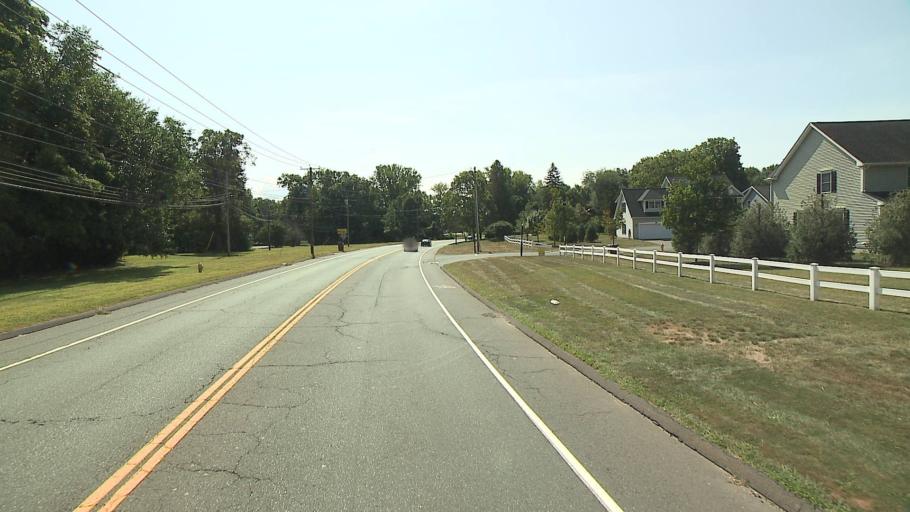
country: US
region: Connecticut
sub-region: Hartford County
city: Windsor Locks
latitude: 41.8998
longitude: -72.6088
